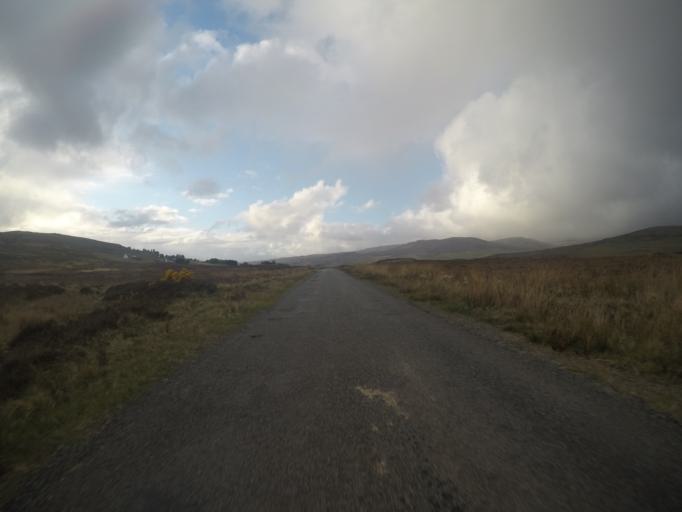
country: GB
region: Scotland
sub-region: Highland
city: Isle of Skye
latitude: 57.4617
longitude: -6.2966
